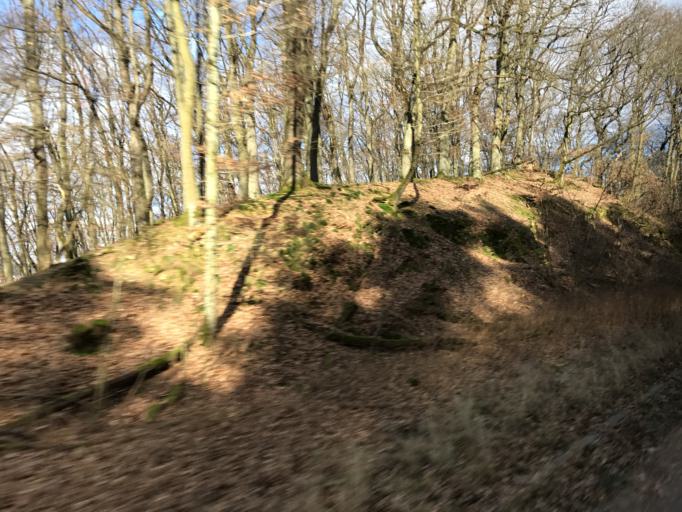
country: DE
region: Hesse
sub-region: Regierungsbezirk Darmstadt
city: Niedernhausen
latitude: 50.1122
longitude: 8.3280
